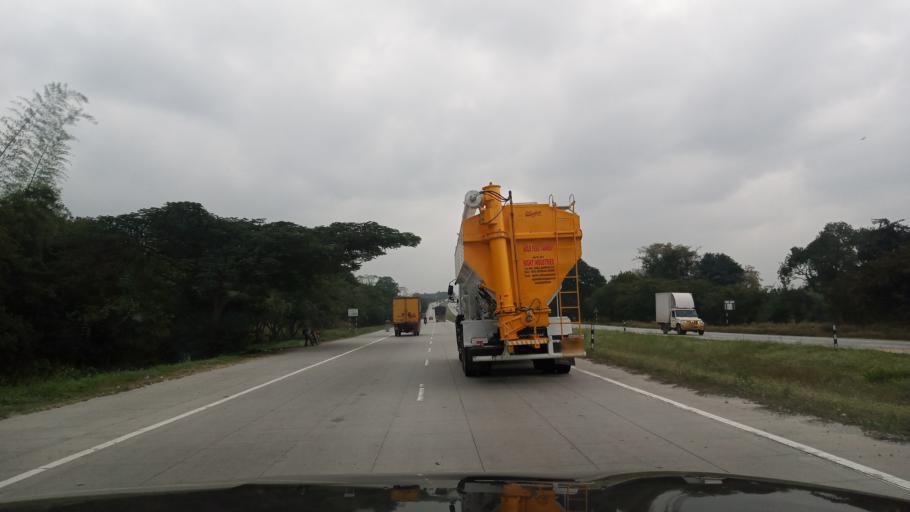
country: IN
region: Karnataka
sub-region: Bangalore Urban
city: Bangalore
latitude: 12.8950
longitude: 77.4771
